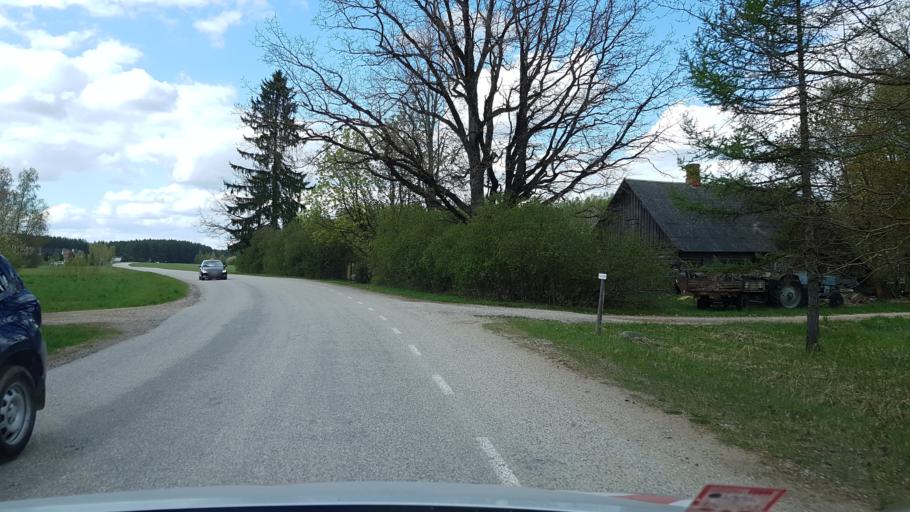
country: EE
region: Tartu
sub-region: Tartu linn
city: Tartu
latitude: 58.3520
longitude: 26.8043
